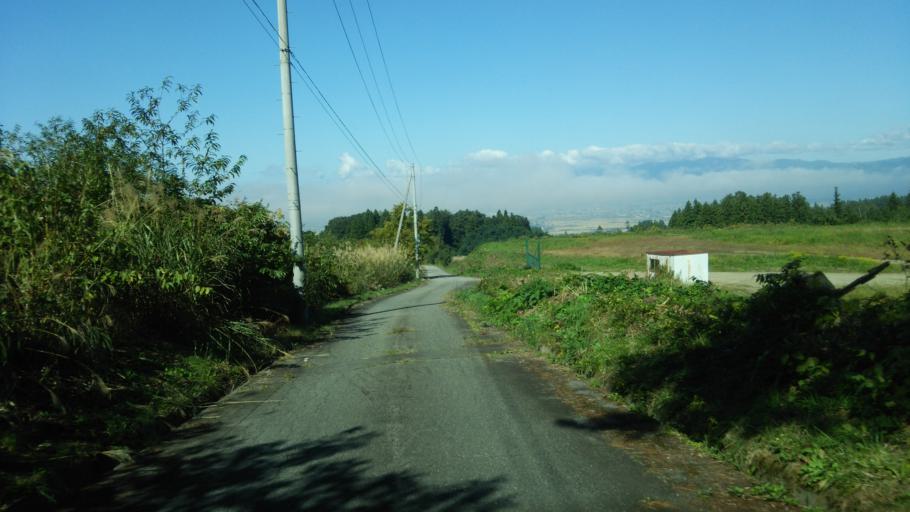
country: JP
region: Fukushima
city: Kitakata
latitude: 37.6120
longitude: 139.9462
